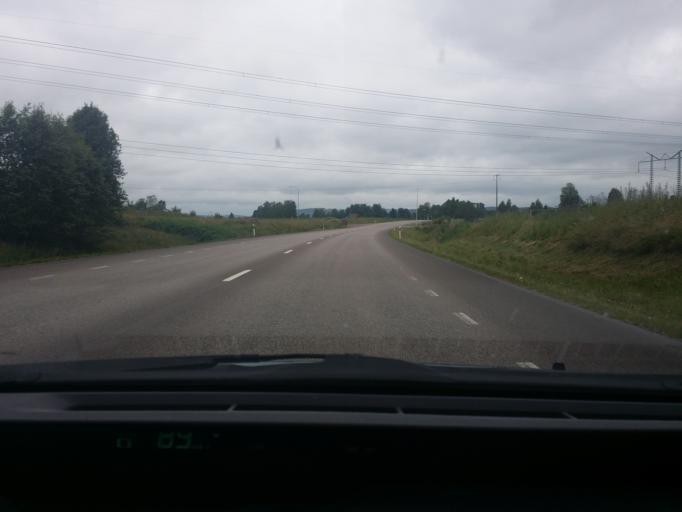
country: SE
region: Dalarna
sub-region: Gagnefs Kommun
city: Djuras
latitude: 60.5509
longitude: 15.1670
